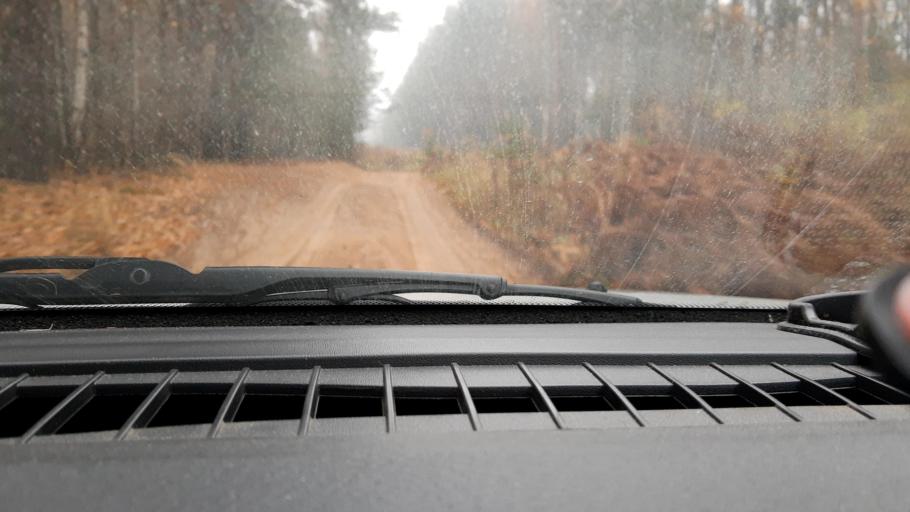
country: RU
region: Nizjnij Novgorod
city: Sitniki
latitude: 56.4285
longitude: 44.0583
